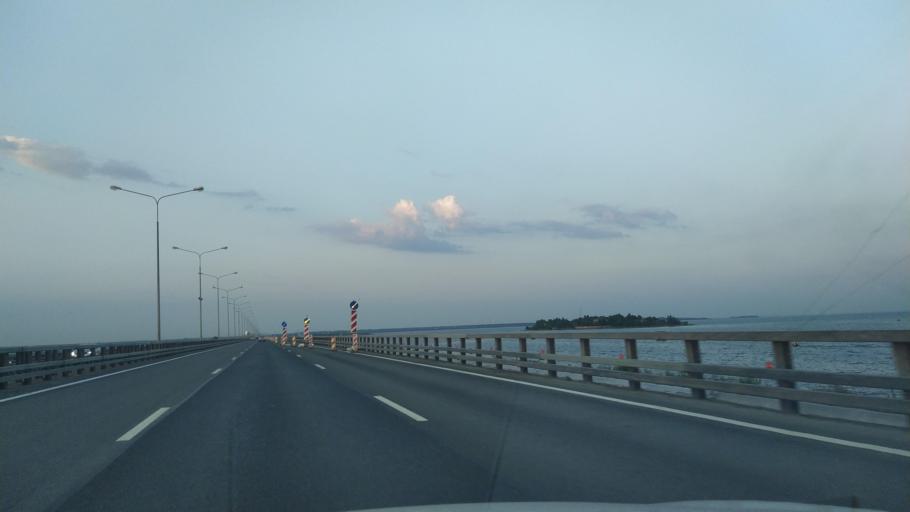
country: RU
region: Leningrad
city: Gorskaya
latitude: 60.0300
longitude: 29.8795
